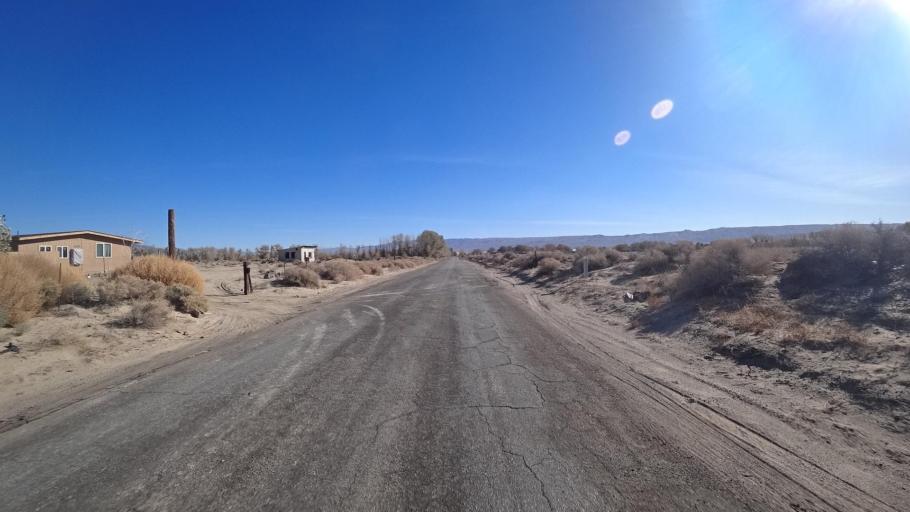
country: US
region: California
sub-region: Kern County
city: California City
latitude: 35.3160
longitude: -117.9342
